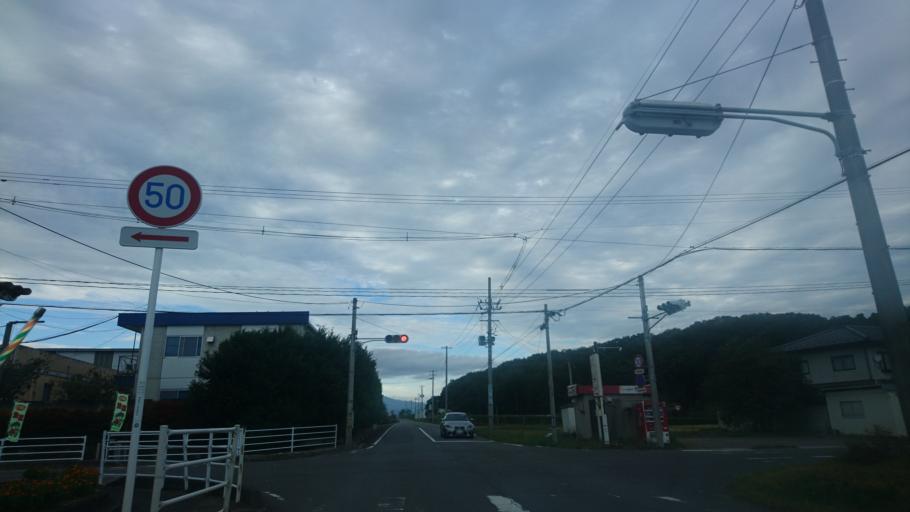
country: JP
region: Fukushima
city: Sukagawa
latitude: 37.3277
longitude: 140.2670
